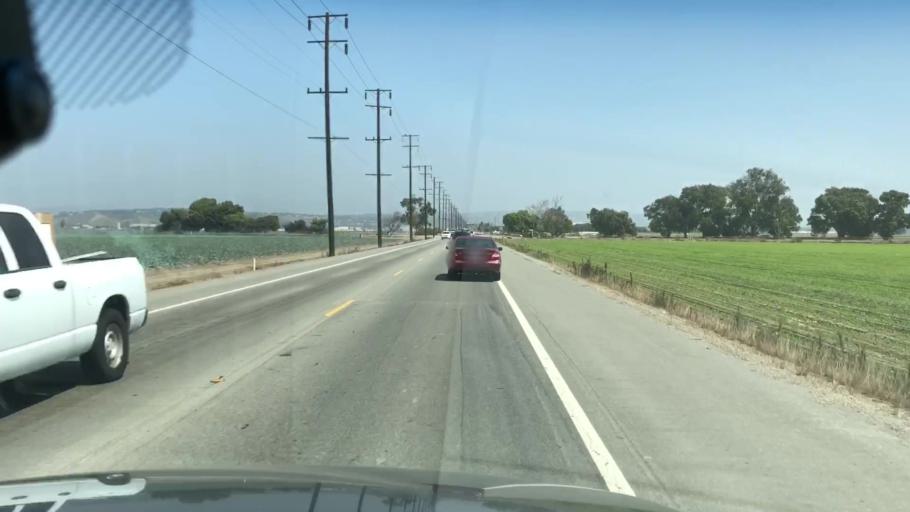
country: US
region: California
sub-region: Ventura County
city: Oxnard
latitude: 34.1907
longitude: -119.1100
